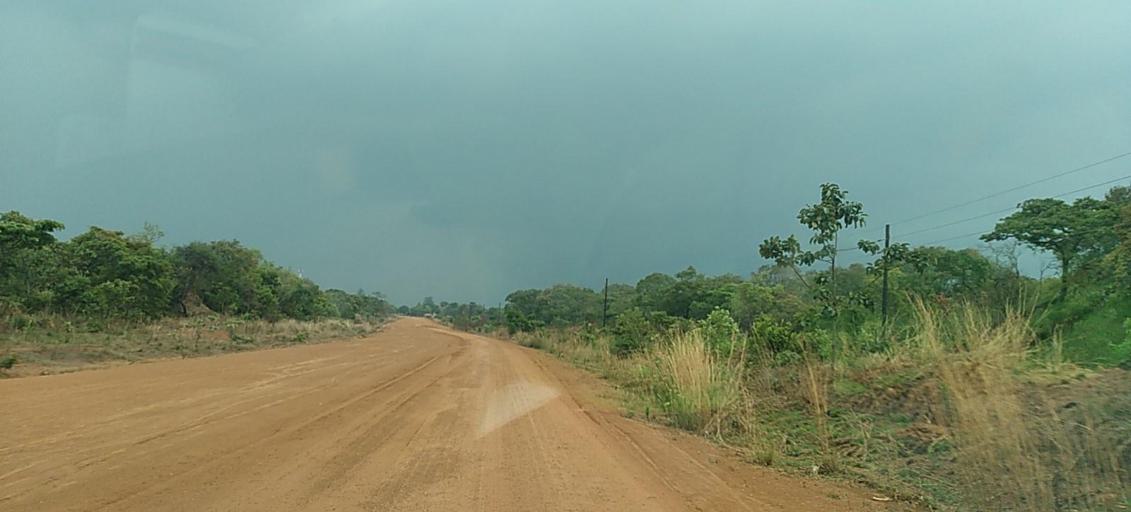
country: ZM
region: North-Western
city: Mwinilunga
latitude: -11.6443
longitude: 24.3990
